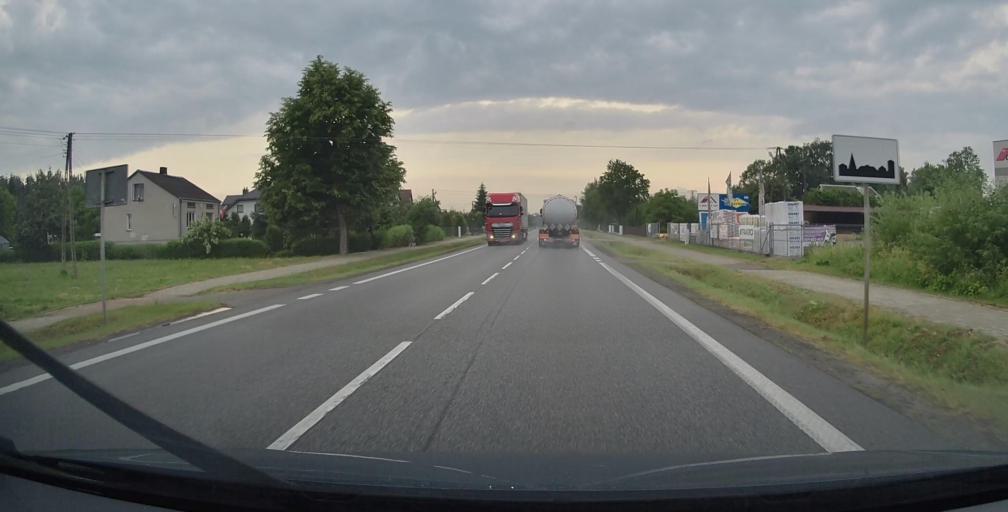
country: PL
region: Masovian Voivodeship
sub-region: Powiat siedlecki
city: Zbuczyn
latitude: 52.0854
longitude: 22.4552
